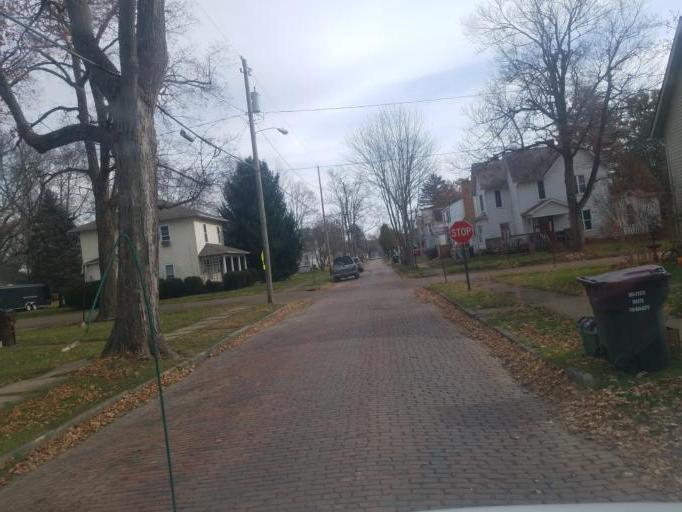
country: US
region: Ohio
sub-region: Knox County
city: Mount Vernon
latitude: 40.3972
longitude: -82.4783
